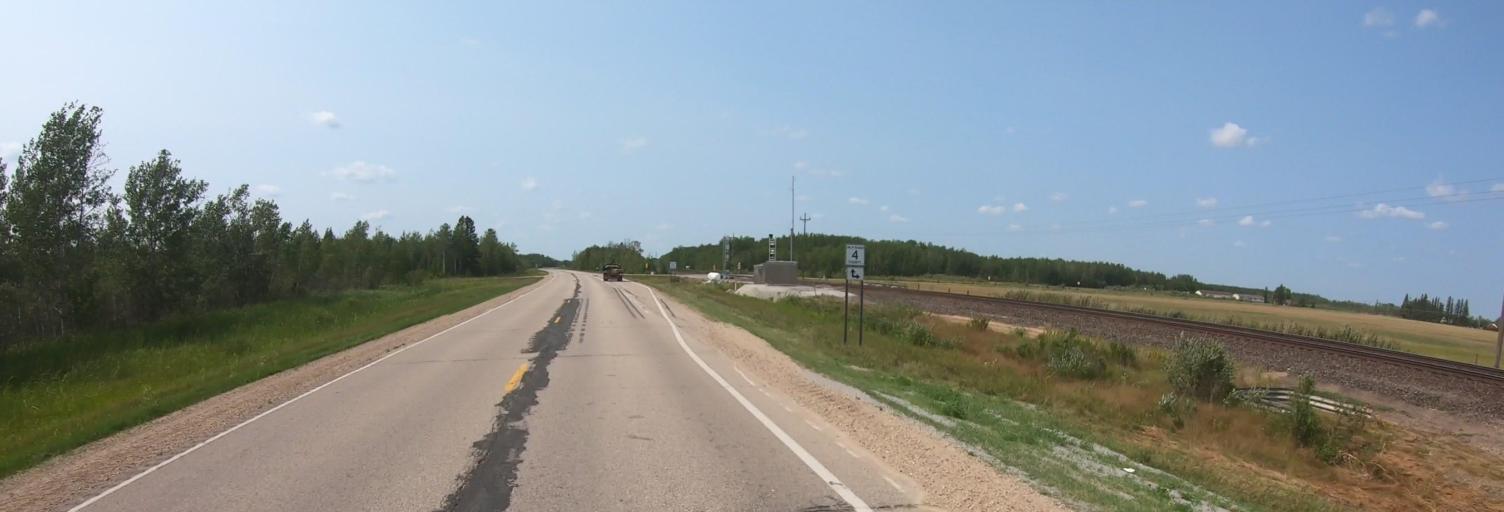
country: US
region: Minnesota
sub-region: Lake of the Woods County
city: Baudette
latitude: 48.7373
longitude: -94.8252
